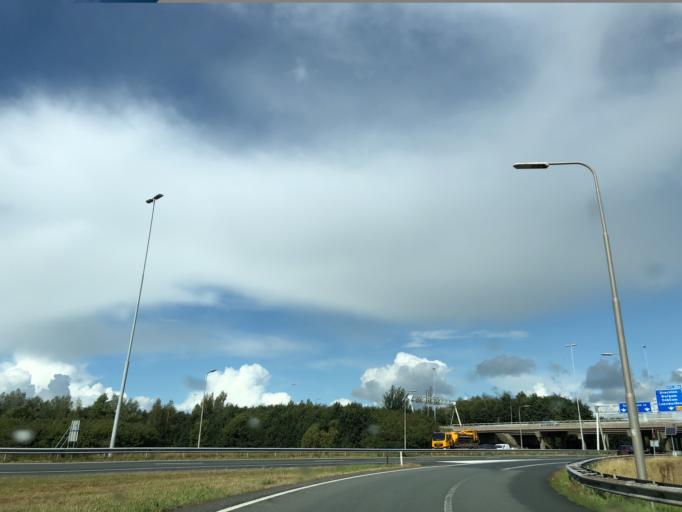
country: NL
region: Friesland
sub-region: Gemeente Smallingerland
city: Drachtstercompagnie
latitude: 53.1038
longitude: 6.1331
